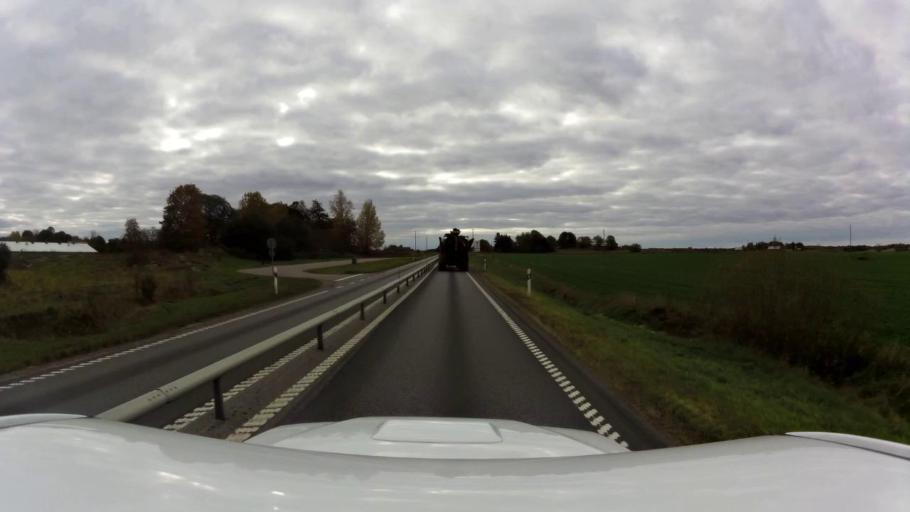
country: SE
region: OEstergoetland
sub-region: Linkopings Kommun
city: Malmslatt
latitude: 58.3443
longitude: 15.5524
